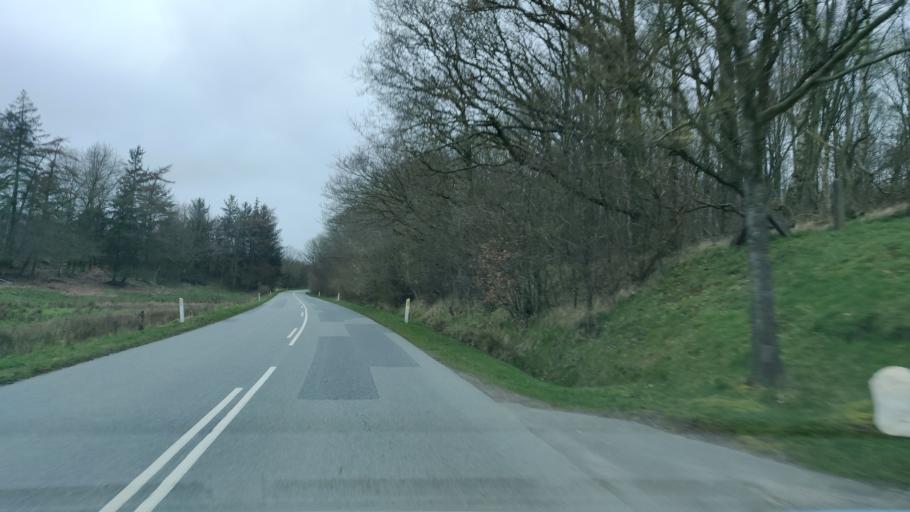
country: DK
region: Central Jutland
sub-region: Skive Kommune
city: Hojslev
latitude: 56.5736
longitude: 9.2354
